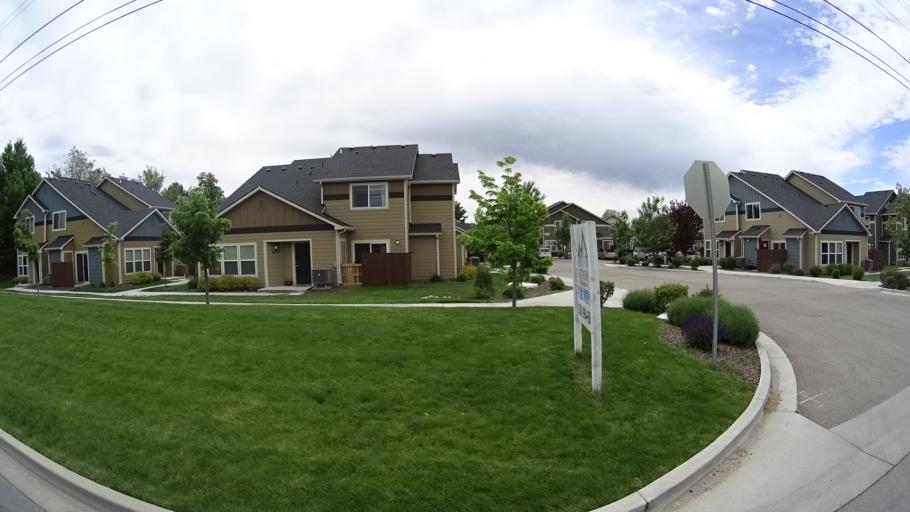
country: US
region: Idaho
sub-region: Ada County
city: Meridian
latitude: 43.5902
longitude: -116.3319
